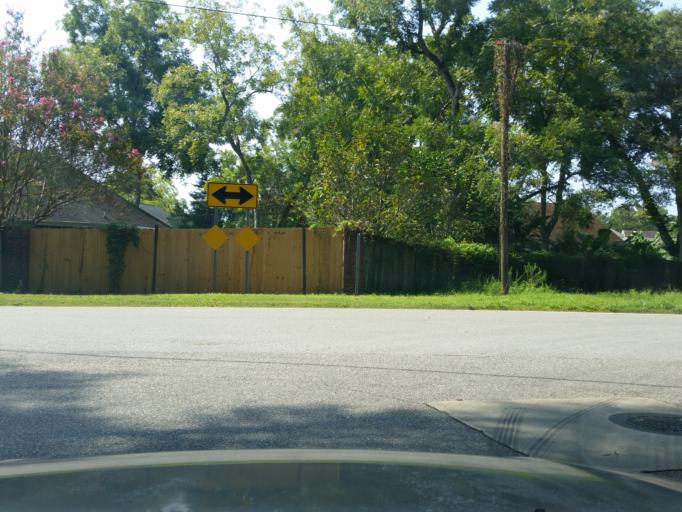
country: US
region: Florida
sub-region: Escambia County
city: Bellview
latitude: 30.4582
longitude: -87.3329
